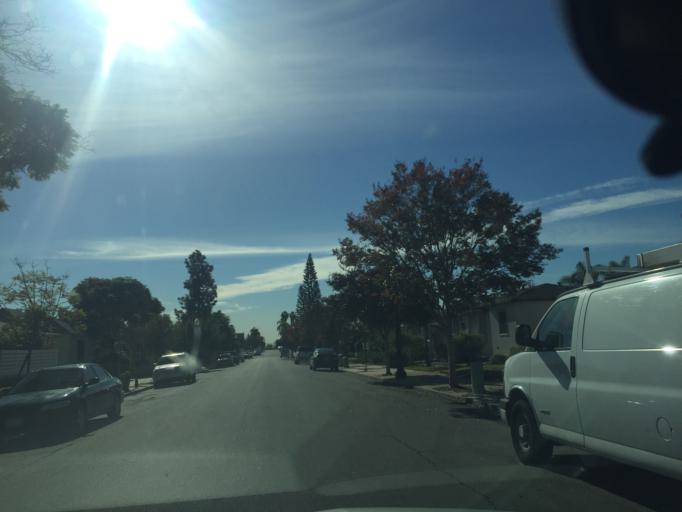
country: US
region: California
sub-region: San Diego County
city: Lemon Grove
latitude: 32.7606
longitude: -117.0889
